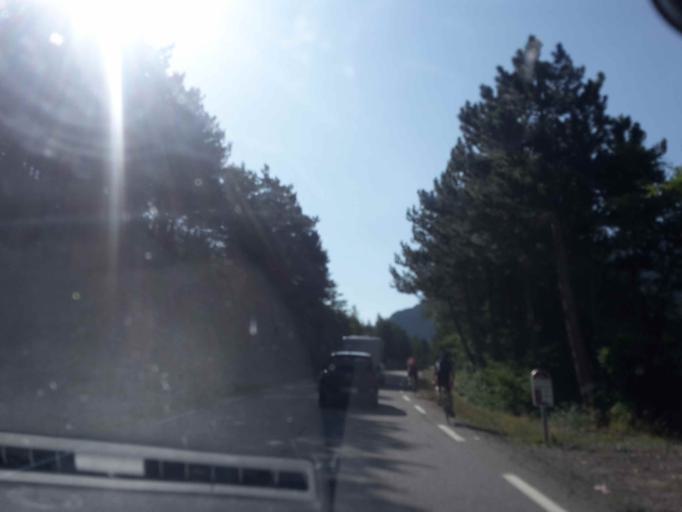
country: FR
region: Provence-Alpes-Cote d'Azur
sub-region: Departement des Hautes-Alpes
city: Guillestre
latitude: 44.6451
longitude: 6.6559
